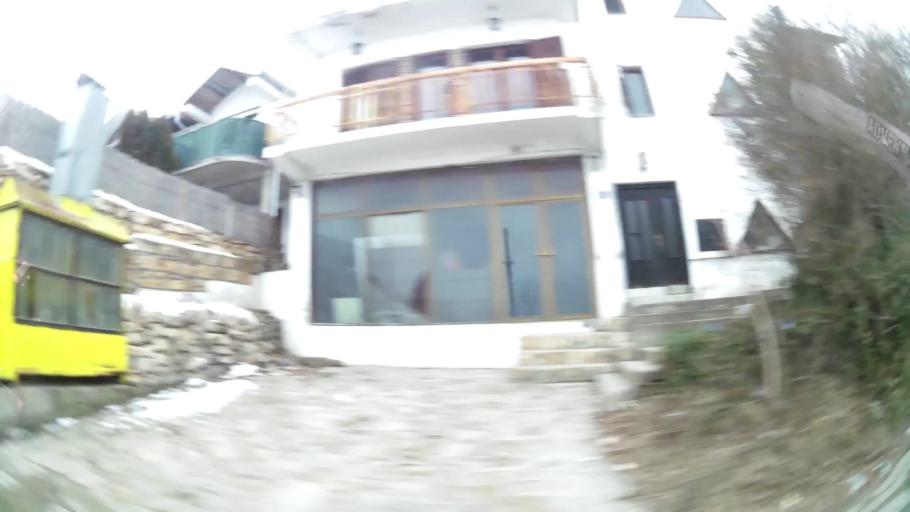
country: MK
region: Saraj
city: Saraj
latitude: 42.0096
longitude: 21.3285
